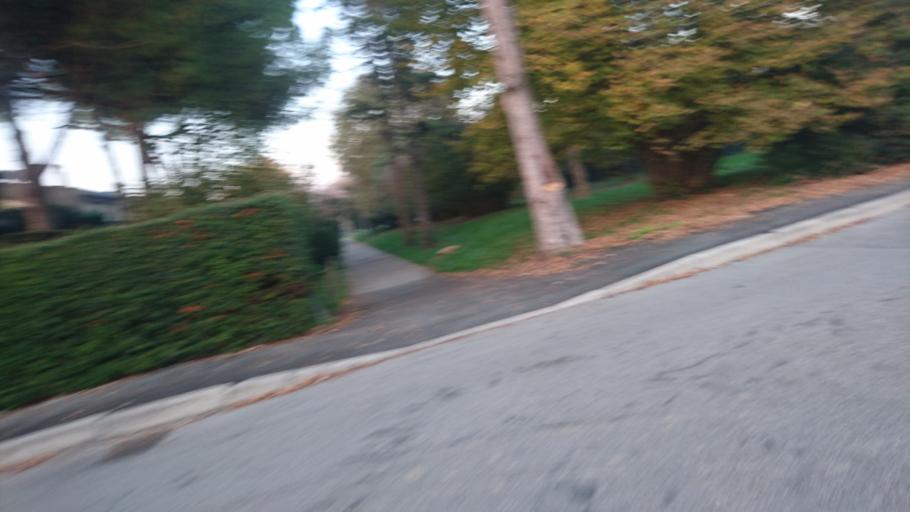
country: IT
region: Veneto
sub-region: Provincia di Padova
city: Mandriola-Sant'Agostino
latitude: 45.3674
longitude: 11.8362
